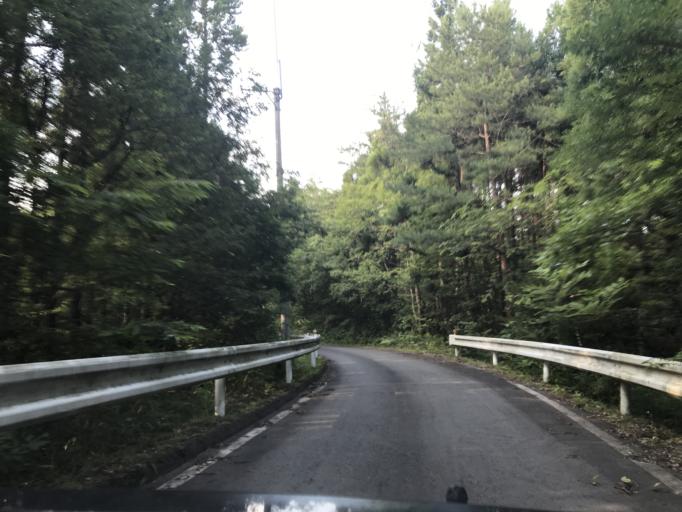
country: JP
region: Iwate
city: Ichinoseki
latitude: 38.8312
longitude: 141.1500
